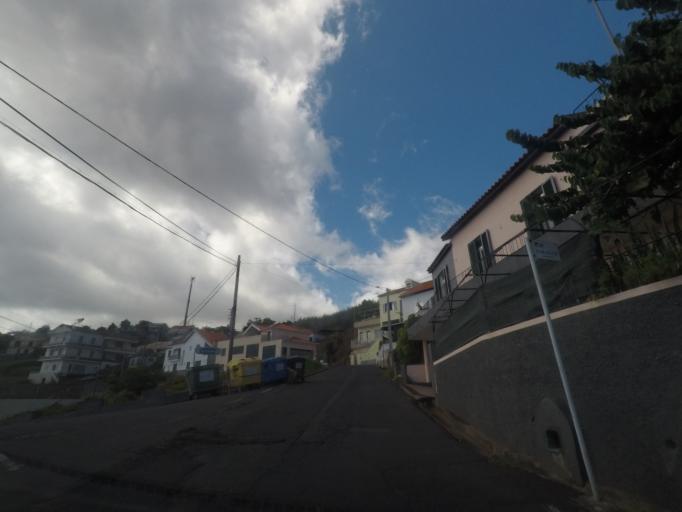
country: PT
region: Madeira
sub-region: Ribeira Brava
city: Campanario
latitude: 32.6732
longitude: -17.0499
